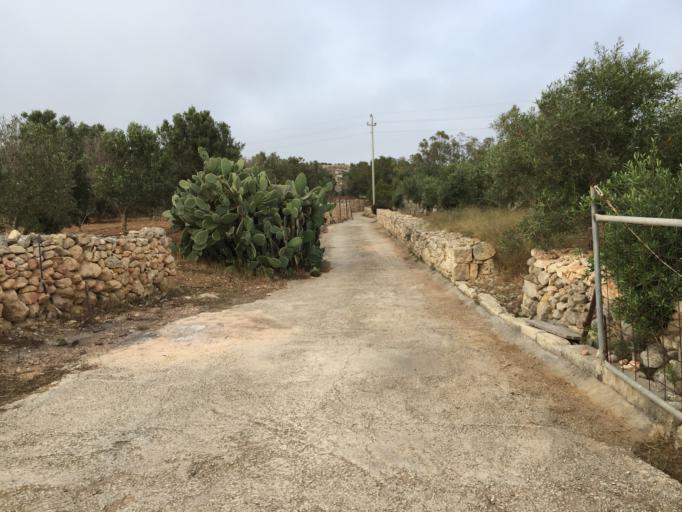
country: MT
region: L-Imgarr
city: Imgarr
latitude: 35.9343
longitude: 14.3857
